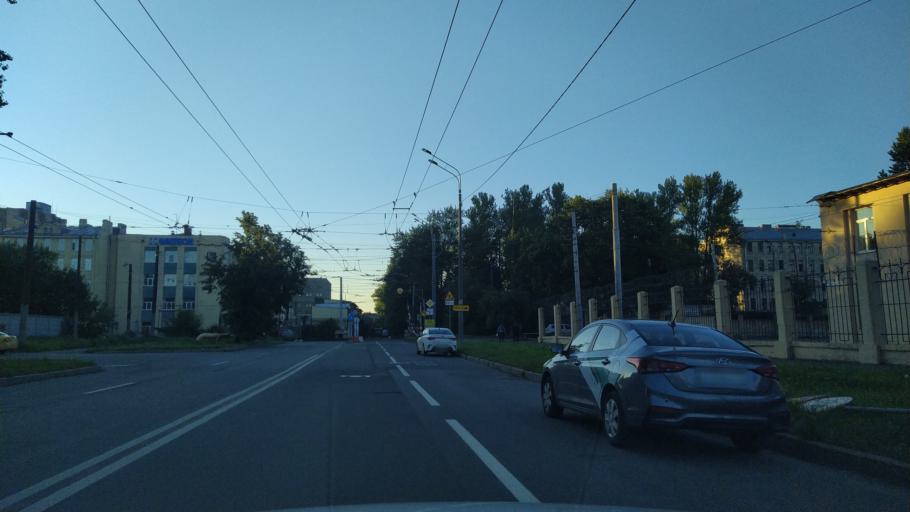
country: RU
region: Leningrad
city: Finlyandskiy
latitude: 59.9698
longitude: 30.3653
